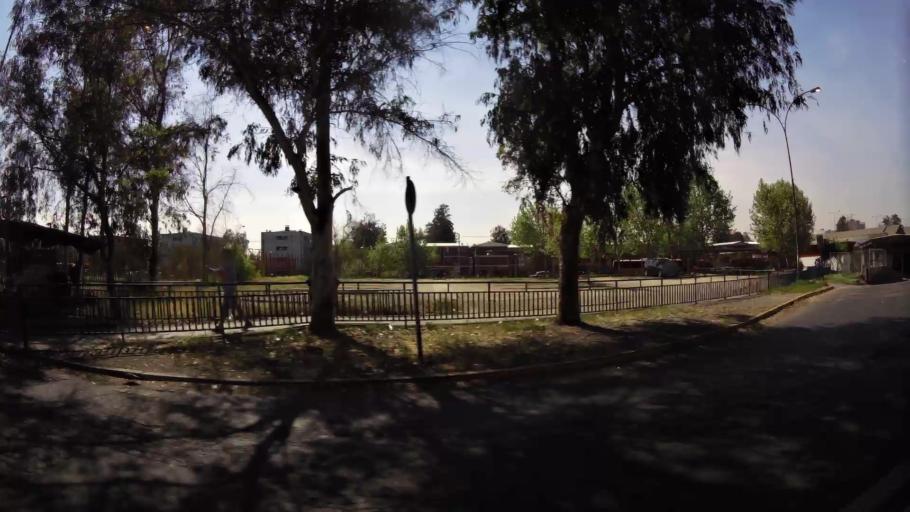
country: CL
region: Santiago Metropolitan
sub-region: Provincia de Santiago
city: Lo Prado
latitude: -33.4577
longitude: -70.7170
